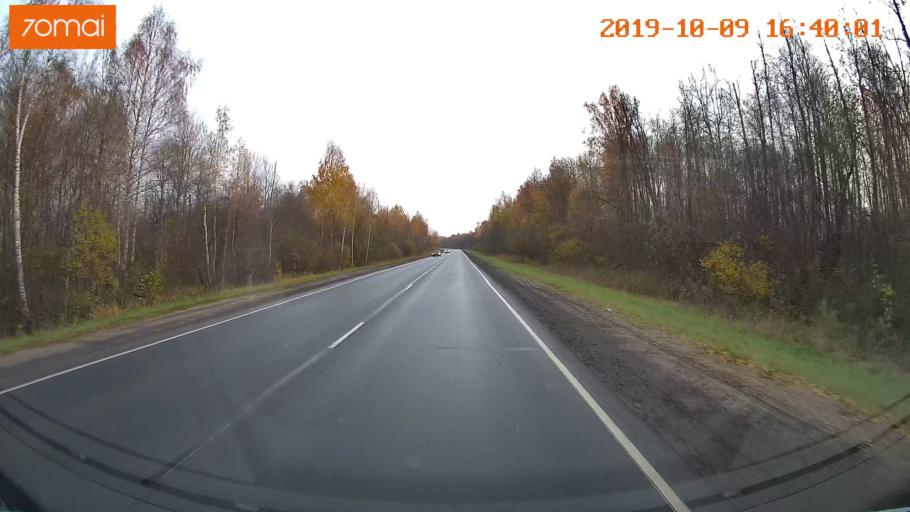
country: RU
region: Kostroma
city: Volgorechensk
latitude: 57.4895
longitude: 41.0555
